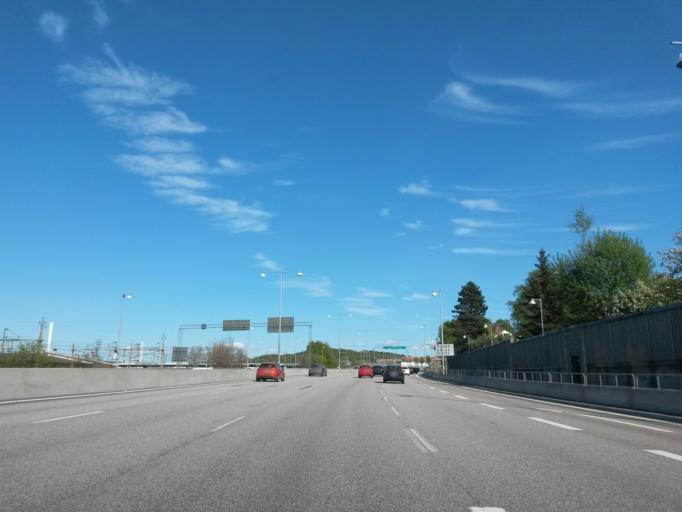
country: SE
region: Vaestra Goetaland
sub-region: Goteborg
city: Goeteborg
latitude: 57.7243
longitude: 12.0166
